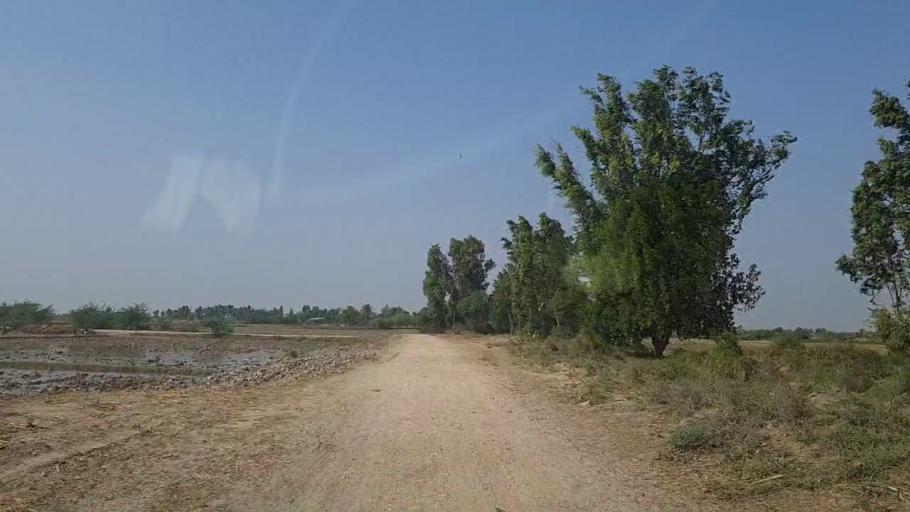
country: PK
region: Sindh
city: Mirpur Sakro
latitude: 24.5669
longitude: 67.8264
